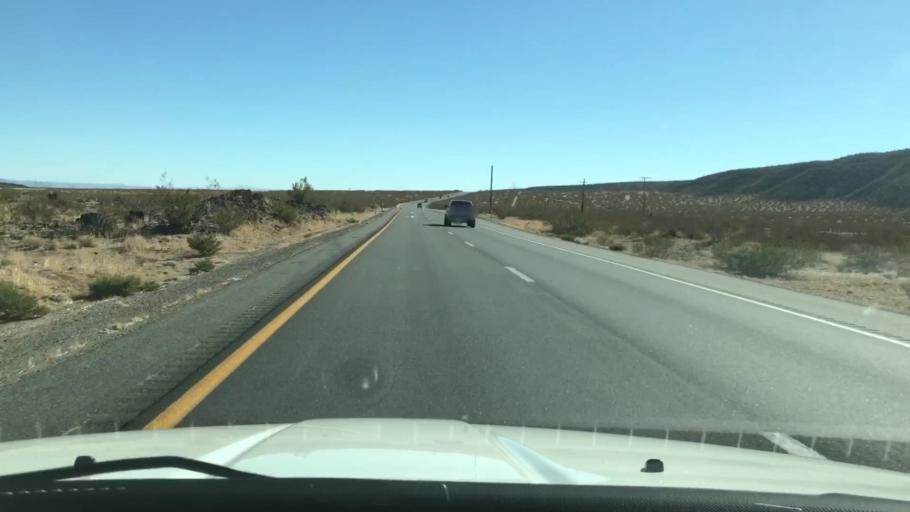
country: US
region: California
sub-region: Kern County
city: Inyokern
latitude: 35.8857
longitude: -117.8933
